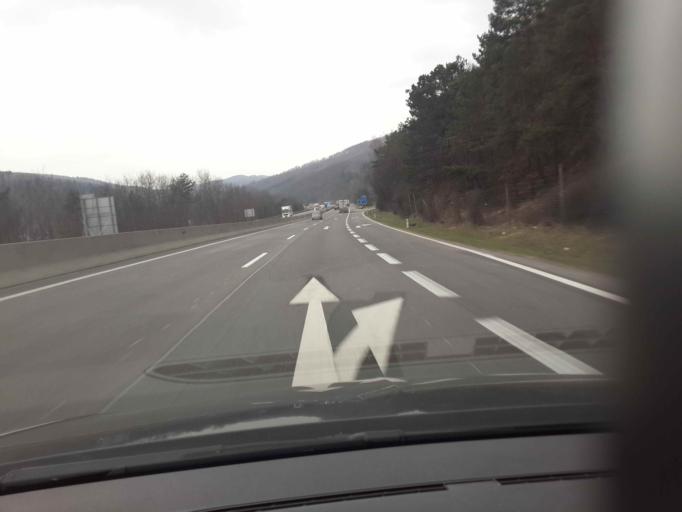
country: AT
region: Lower Austria
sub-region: Politischer Bezirk Baden
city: Alland
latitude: 48.0652
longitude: 16.0700
